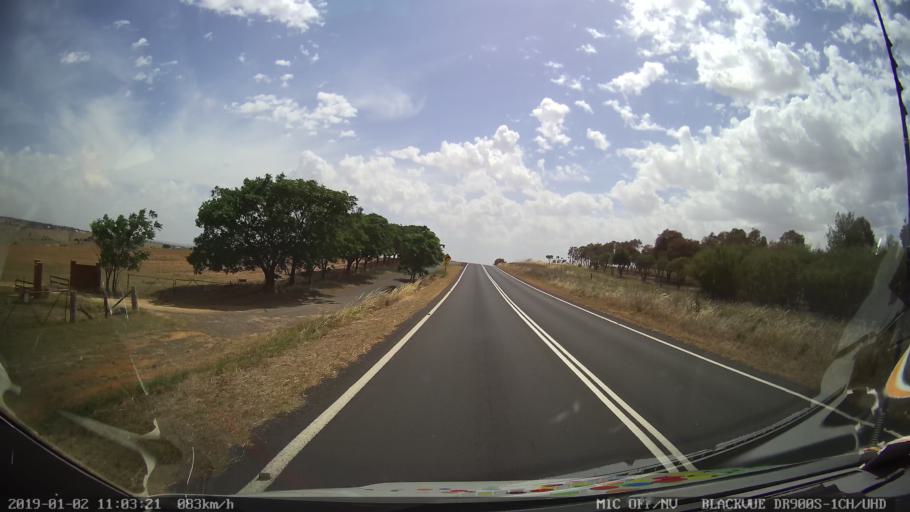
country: AU
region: New South Wales
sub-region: Young
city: Young
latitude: -34.5784
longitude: 148.3371
